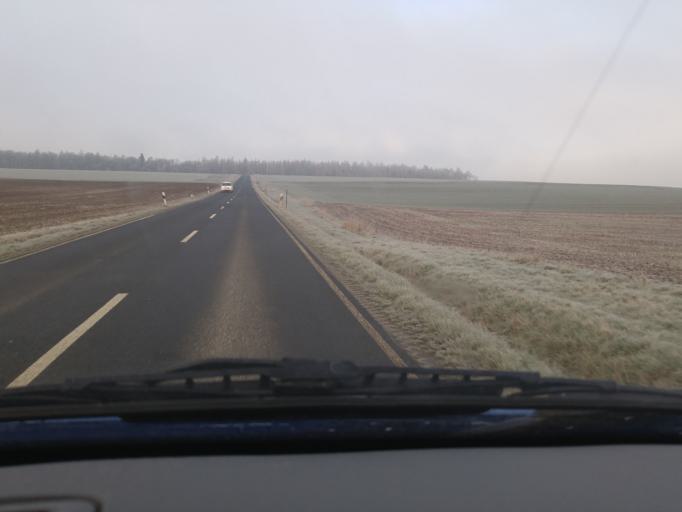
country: DE
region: Hesse
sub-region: Regierungsbezirk Darmstadt
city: Karben
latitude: 50.2698
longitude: 8.7526
